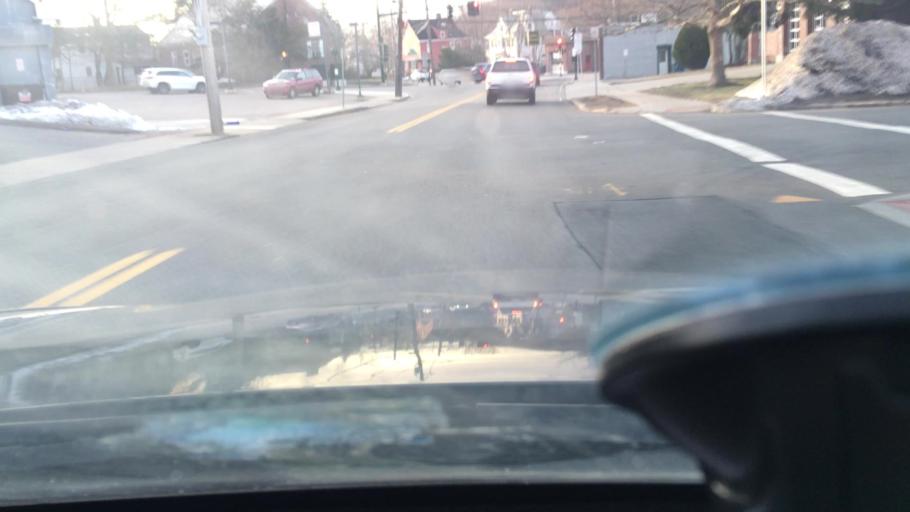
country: US
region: Massachusetts
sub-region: Middlesex County
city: Watertown
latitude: 42.3780
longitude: -71.1886
